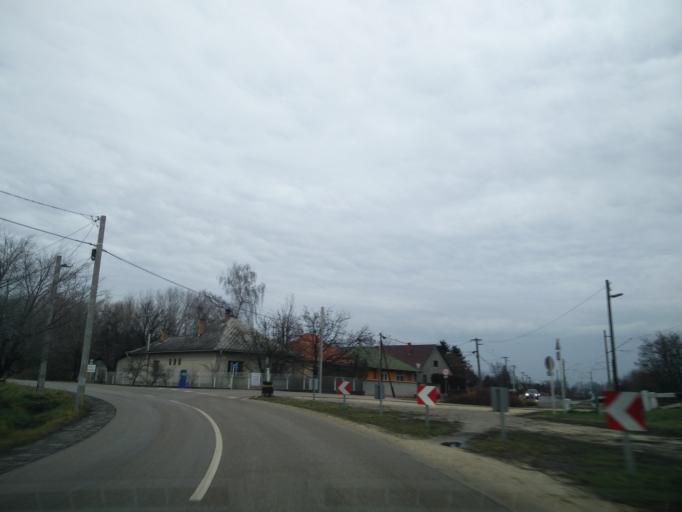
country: HU
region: Pest
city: Suelysap
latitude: 47.4530
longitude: 19.5438
